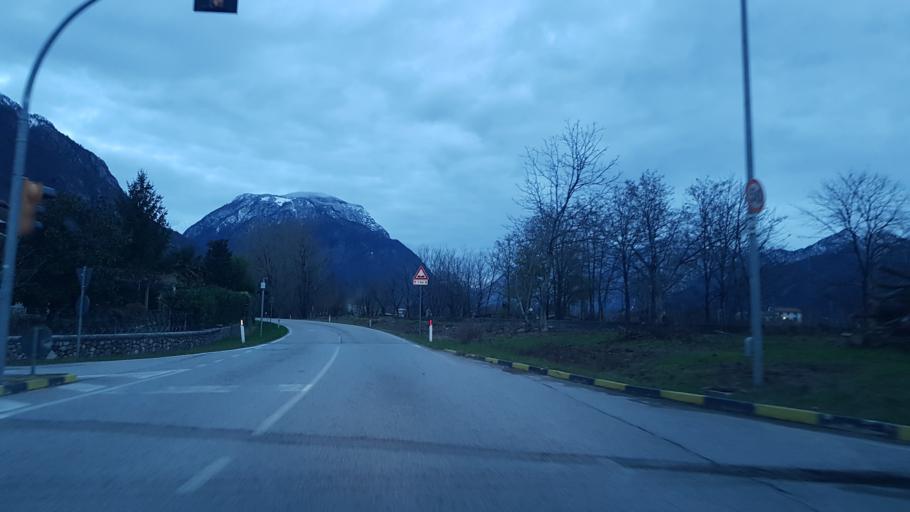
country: IT
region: Friuli Venezia Giulia
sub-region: Provincia di Udine
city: Gemona
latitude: 46.2763
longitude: 13.1002
